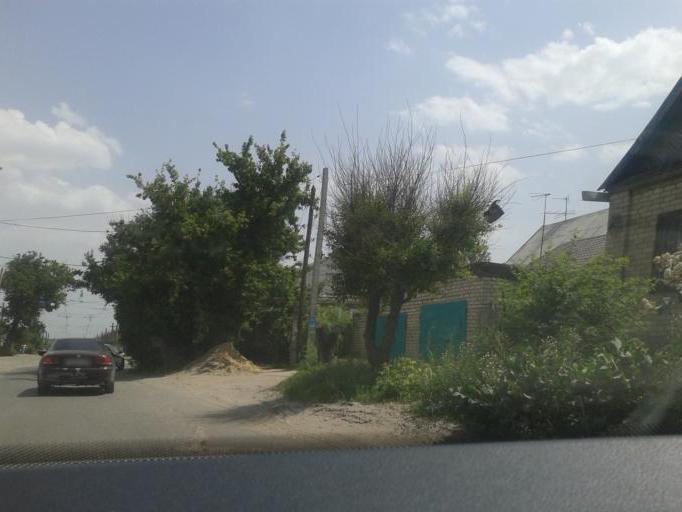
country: RU
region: Volgograd
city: Volgograd
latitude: 48.6929
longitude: 44.4545
